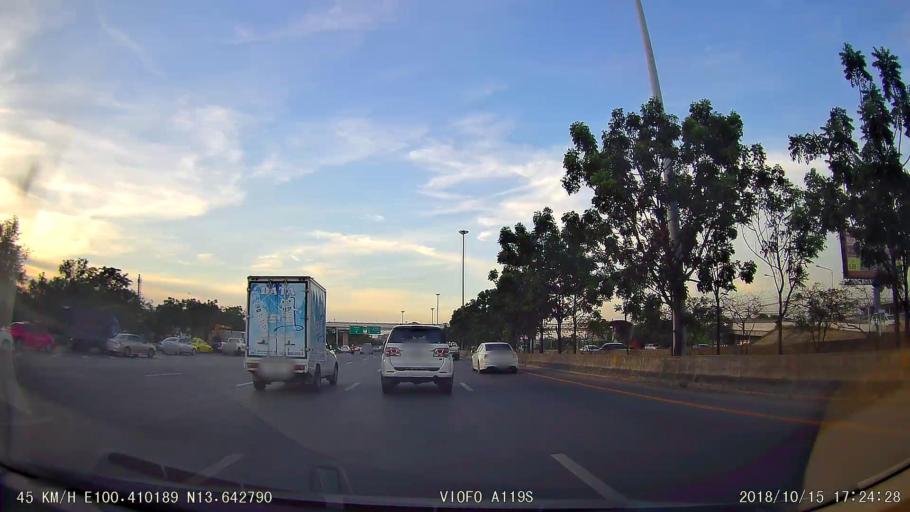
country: TH
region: Bangkok
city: Bang Bon
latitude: 13.6430
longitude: 100.4101
